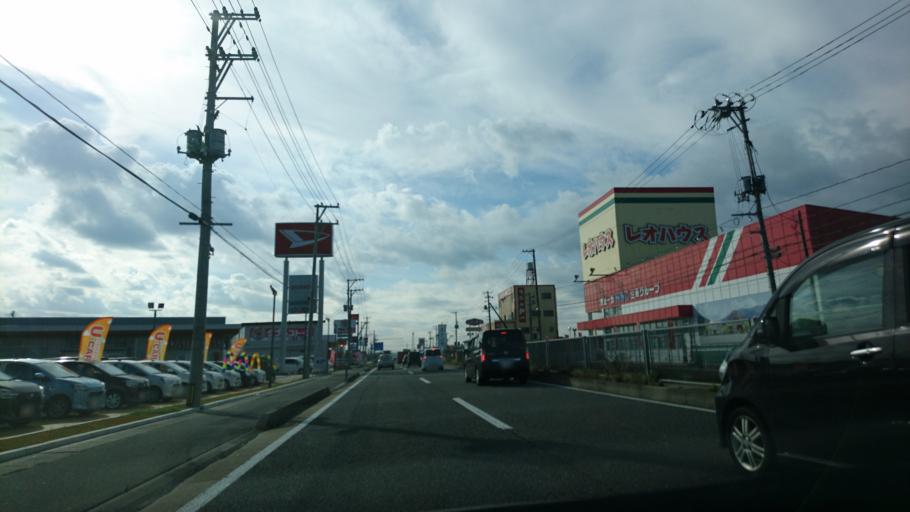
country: JP
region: Miyagi
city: Furukawa
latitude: 38.5775
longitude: 140.9460
